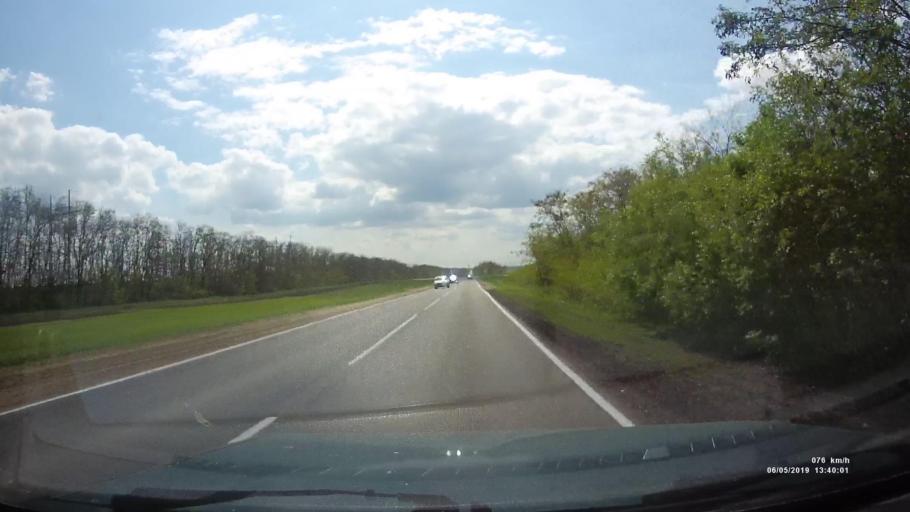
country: RU
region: Rostov
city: Ust'-Donetskiy
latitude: 47.6694
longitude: 40.6979
